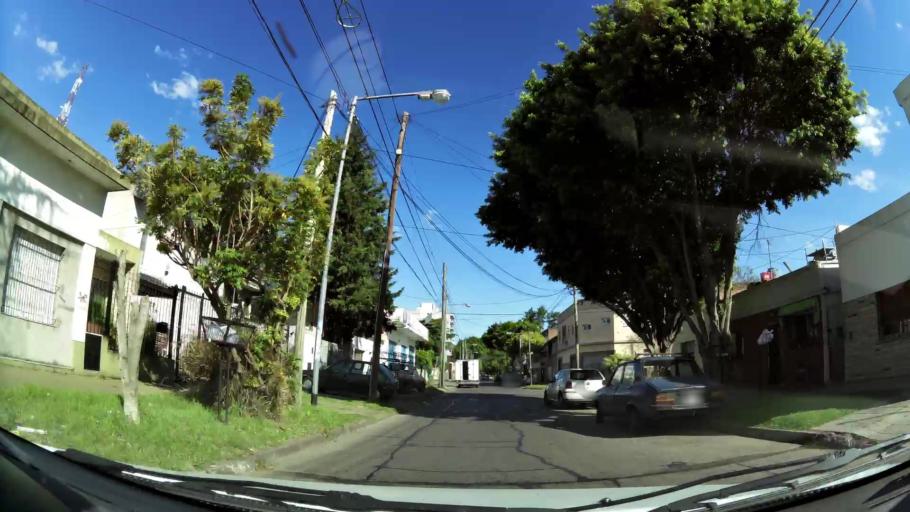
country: AR
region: Buenos Aires
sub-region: Partido de General San Martin
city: General San Martin
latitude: -34.5421
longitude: -58.5544
